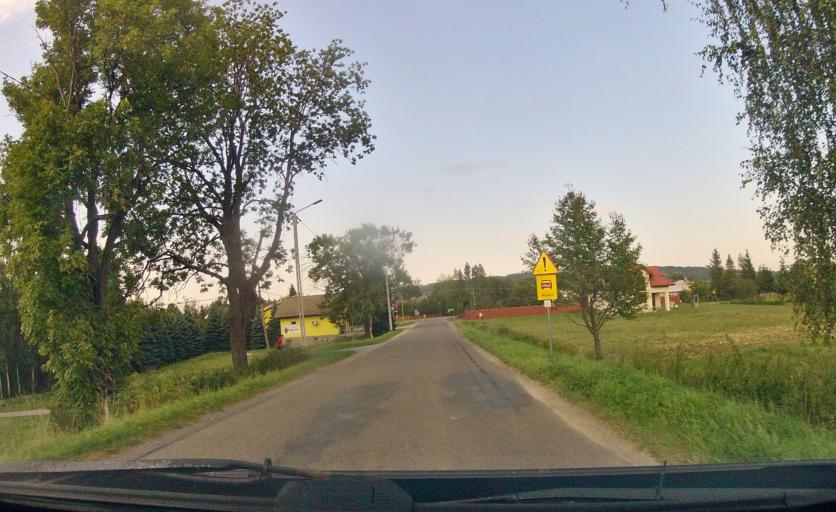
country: PL
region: Subcarpathian Voivodeship
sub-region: Powiat krosnienski
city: Dukla
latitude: 49.5573
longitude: 21.6262
